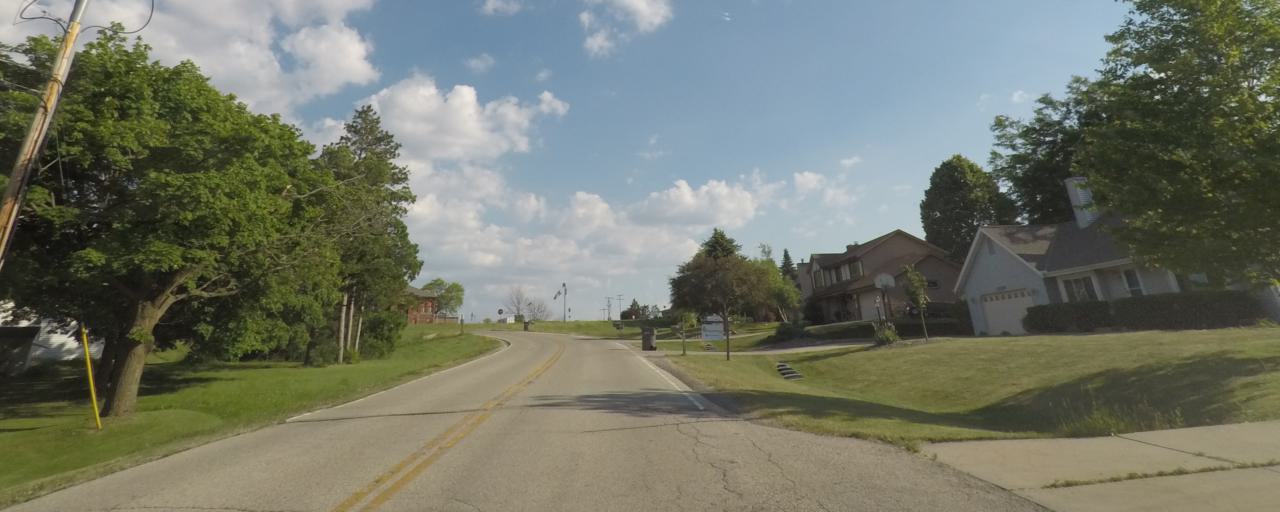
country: US
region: Wisconsin
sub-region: Waukesha County
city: Muskego
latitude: 42.9234
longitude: -88.0996
